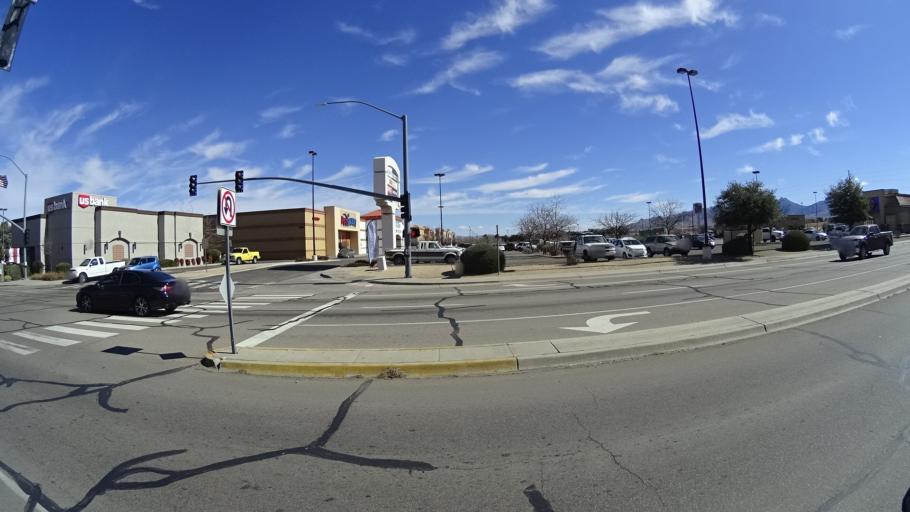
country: US
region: Arizona
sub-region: Mohave County
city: Kingman
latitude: 35.2205
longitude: -114.0361
